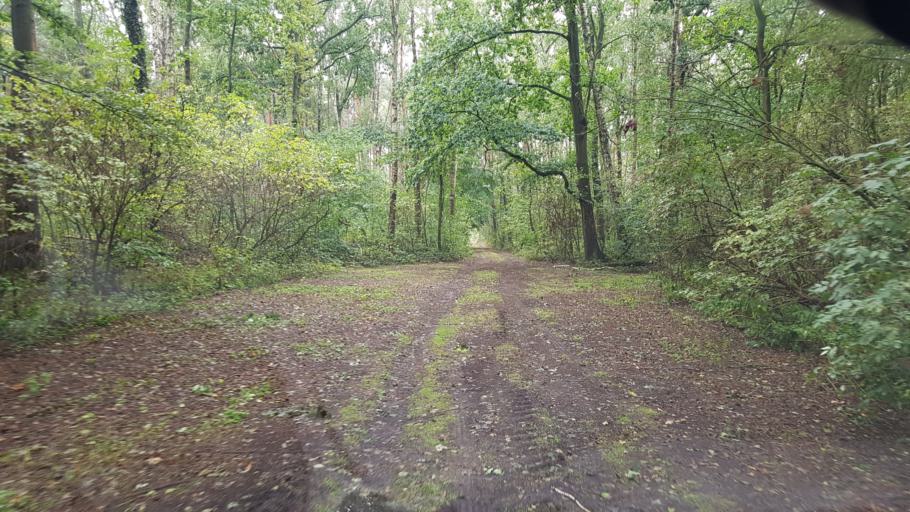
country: DE
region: Brandenburg
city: Ruckersdorf
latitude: 51.5996
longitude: 13.5643
